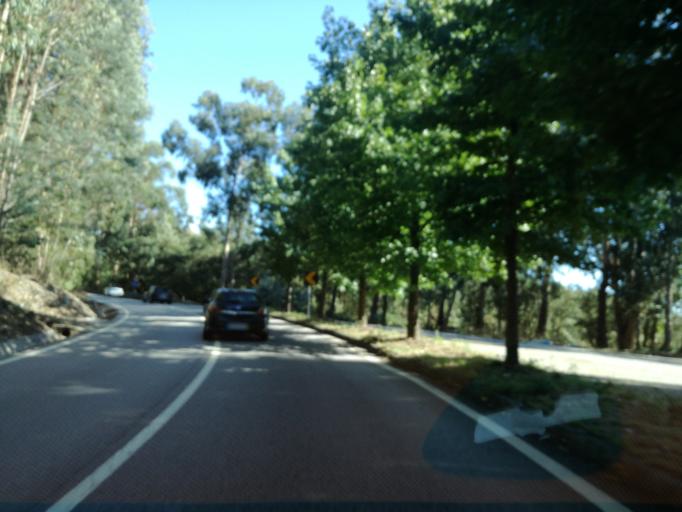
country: PT
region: Porto
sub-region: Pacos de Ferreira
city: Seroa
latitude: 41.2584
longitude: -8.4574
